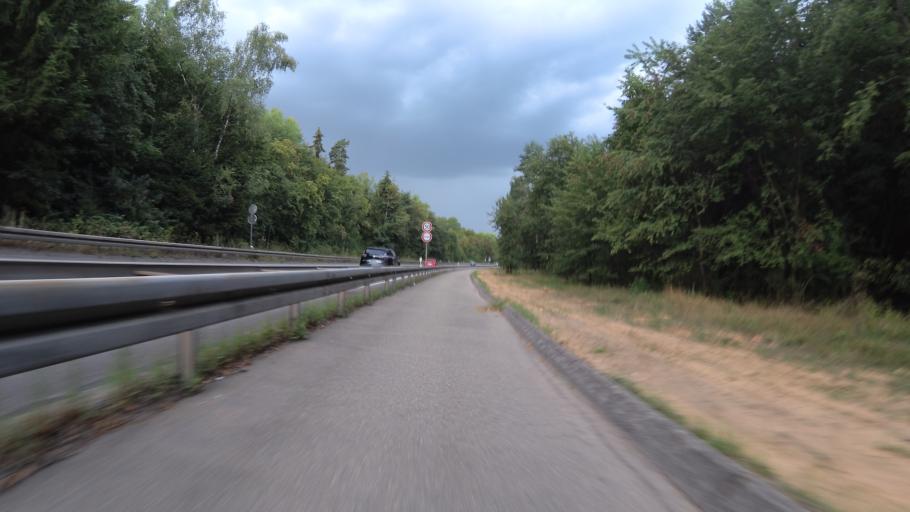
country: DE
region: Saarland
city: Bexbach
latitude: 49.3335
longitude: 7.2289
